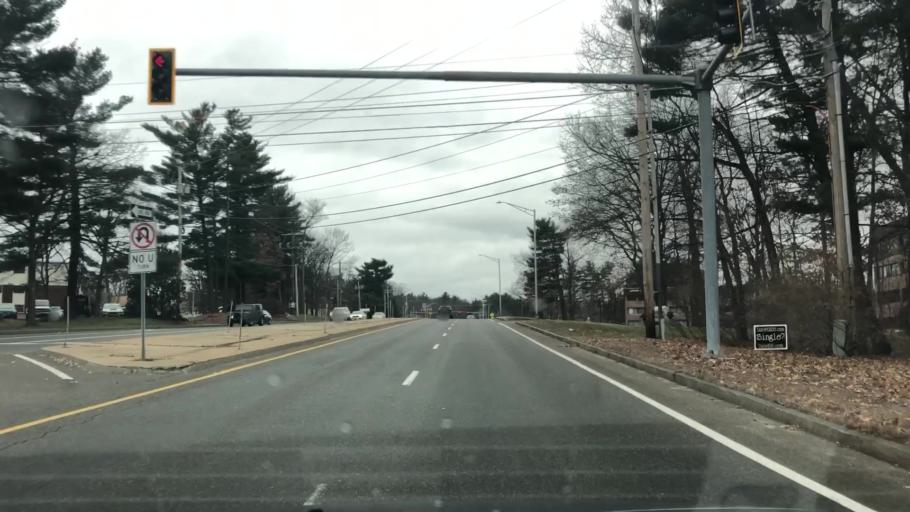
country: US
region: Massachusetts
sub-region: Middlesex County
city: Tyngsboro
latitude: 42.7080
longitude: -71.4521
